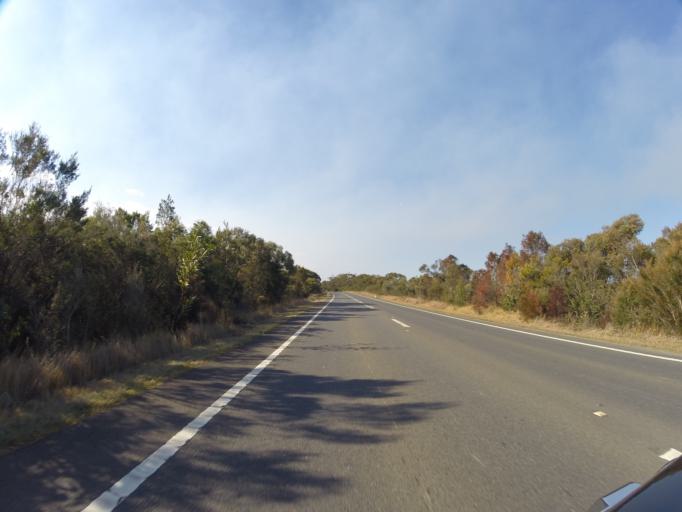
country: AU
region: New South Wales
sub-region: Sutherland Shire
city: Menai
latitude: -34.0166
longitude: 150.9814
